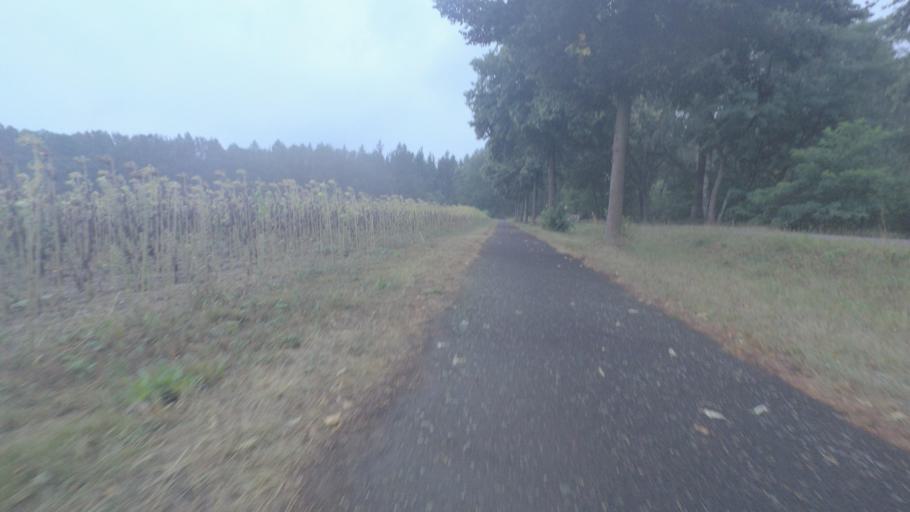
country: DE
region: Brandenburg
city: Heiligengrabe
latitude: 53.1338
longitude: 12.3717
